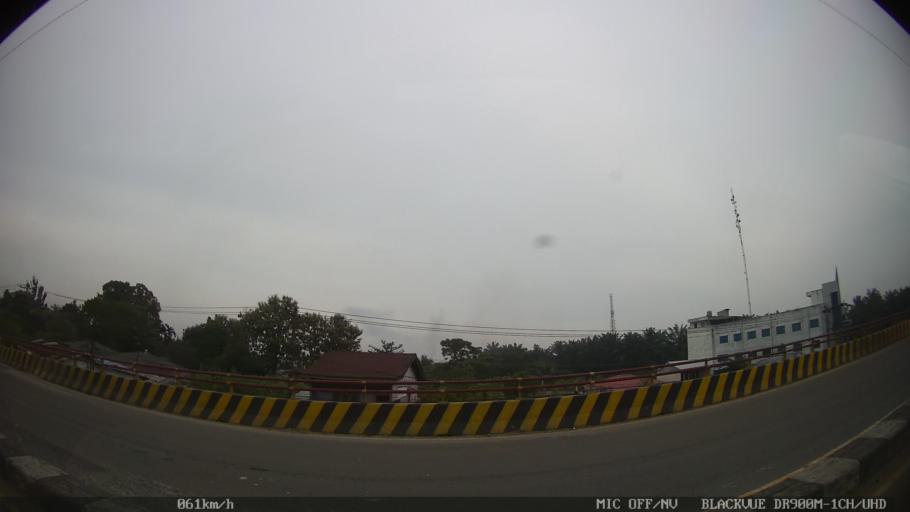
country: ID
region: North Sumatra
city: Deli Tua
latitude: 3.5358
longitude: 98.7198
